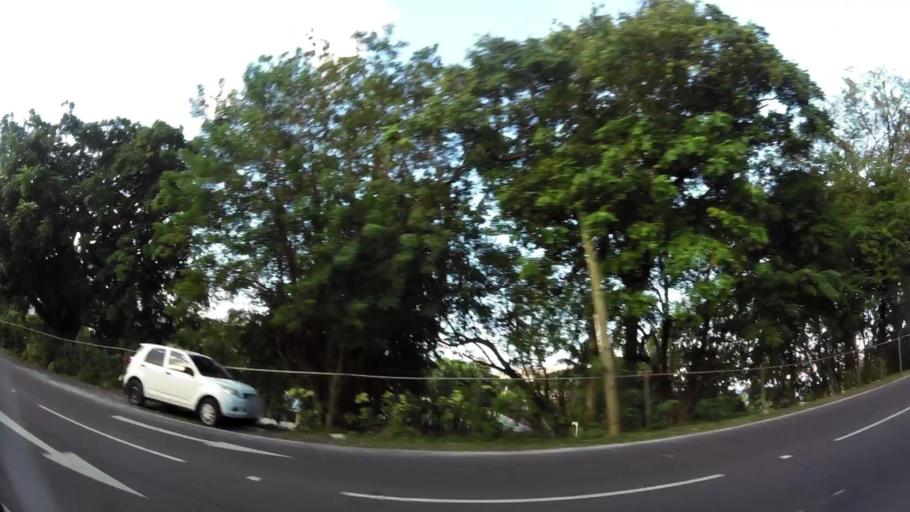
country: LC
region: Castries Quarter
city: Bisee
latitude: 14.0403
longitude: -60.9695
